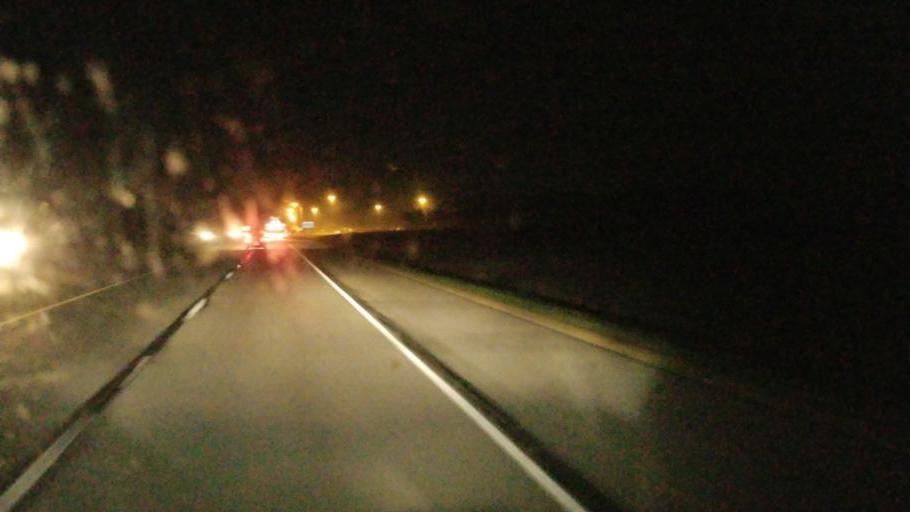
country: US
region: Indiana
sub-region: DeKalb County
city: Garrett
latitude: 41.2885
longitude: -85.0871
